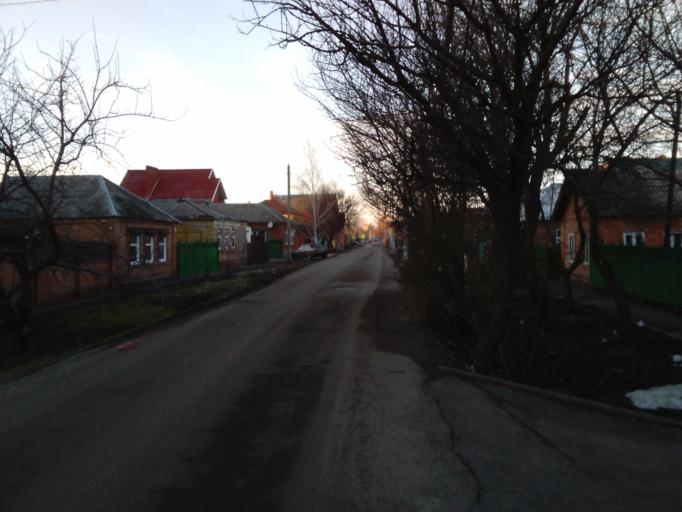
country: RU
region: Rostov
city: Bataysk
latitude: 47.1433
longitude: 39.7437
